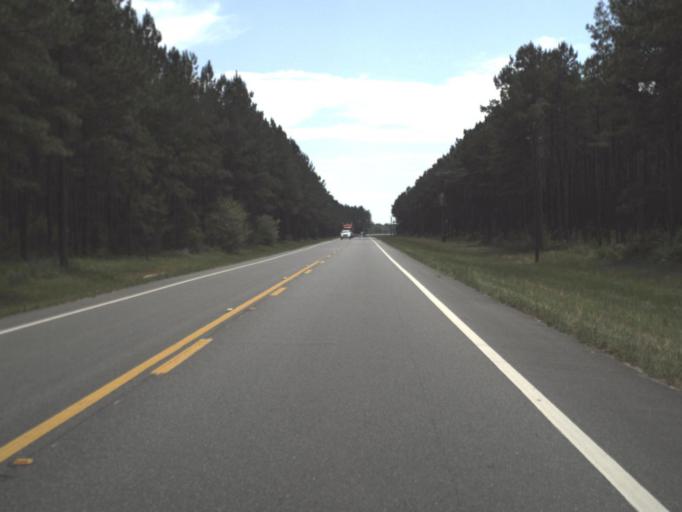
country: US
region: Florida
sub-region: Gulf County
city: Wewahitchka
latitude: 30.2334
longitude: -85.2074
